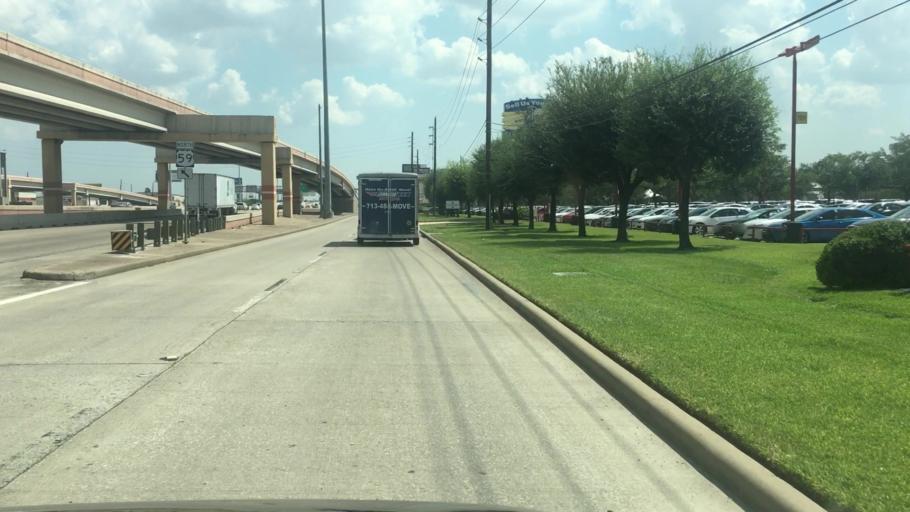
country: US
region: Texas
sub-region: Fort Bend County
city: Meadows Place
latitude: 29.6458
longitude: -95.5735
